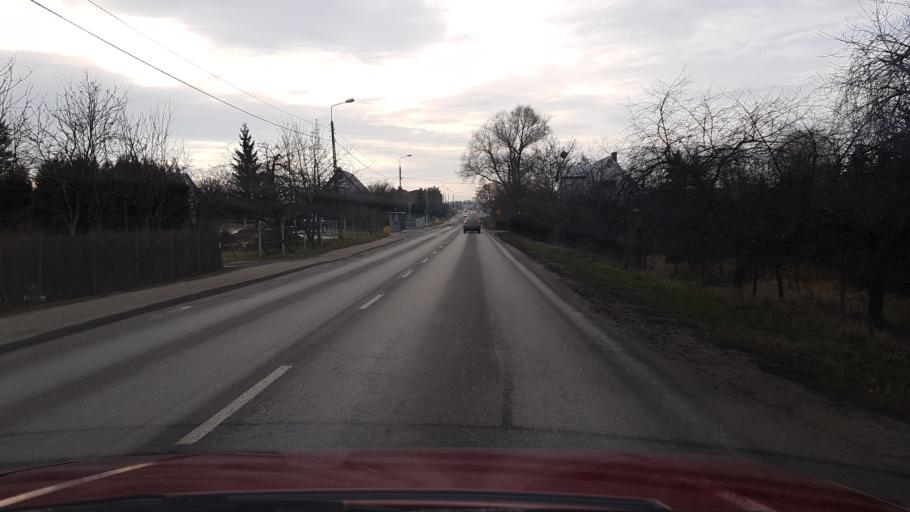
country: PL
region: West Pomeranian Voivodeship
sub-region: Powiat policki
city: Police
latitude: 53.5183
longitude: 14.5679
